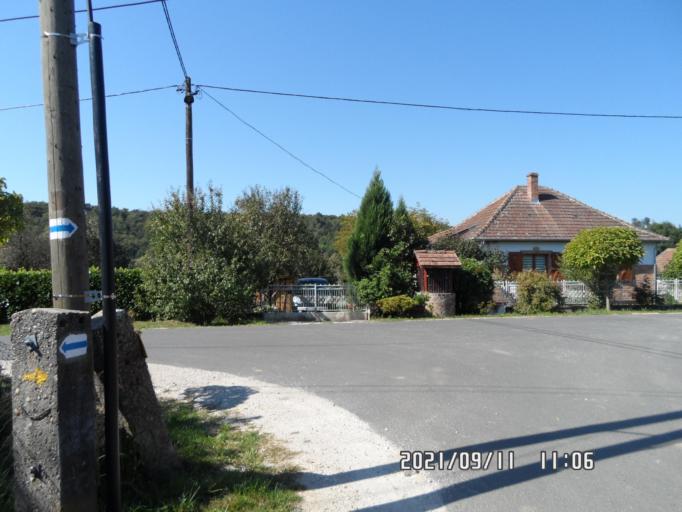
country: HU
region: Zala
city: Zalaegerszeg
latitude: 46.7359
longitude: 16.7168
